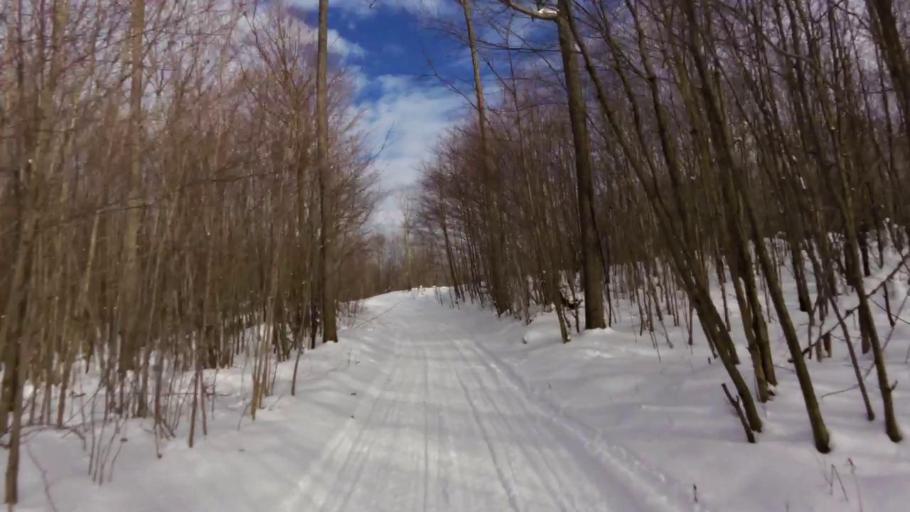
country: US
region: Pennsylvania
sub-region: McKean County
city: Foster Brook
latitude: 42.0050
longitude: -78.5742
